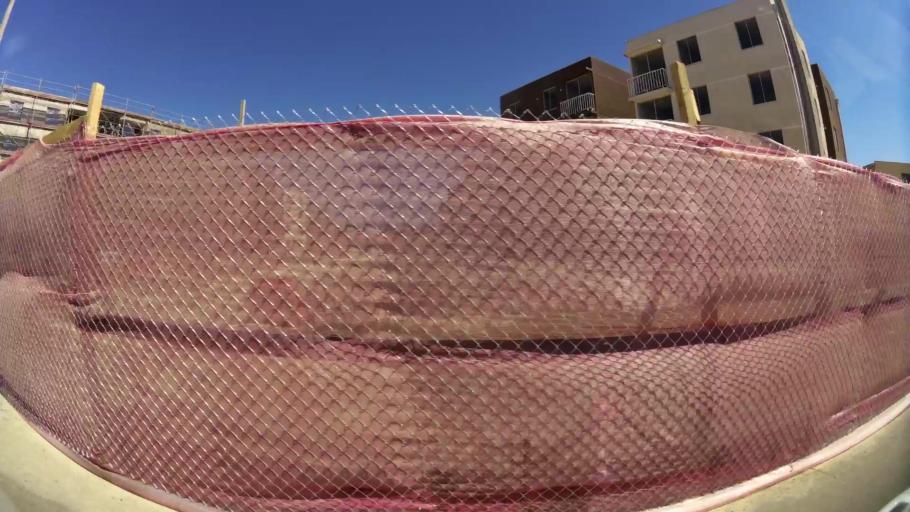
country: CL
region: O'Higgins
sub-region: Provincia de Cachapoal
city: Rancagua
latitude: -34.1708
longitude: -70.7791
